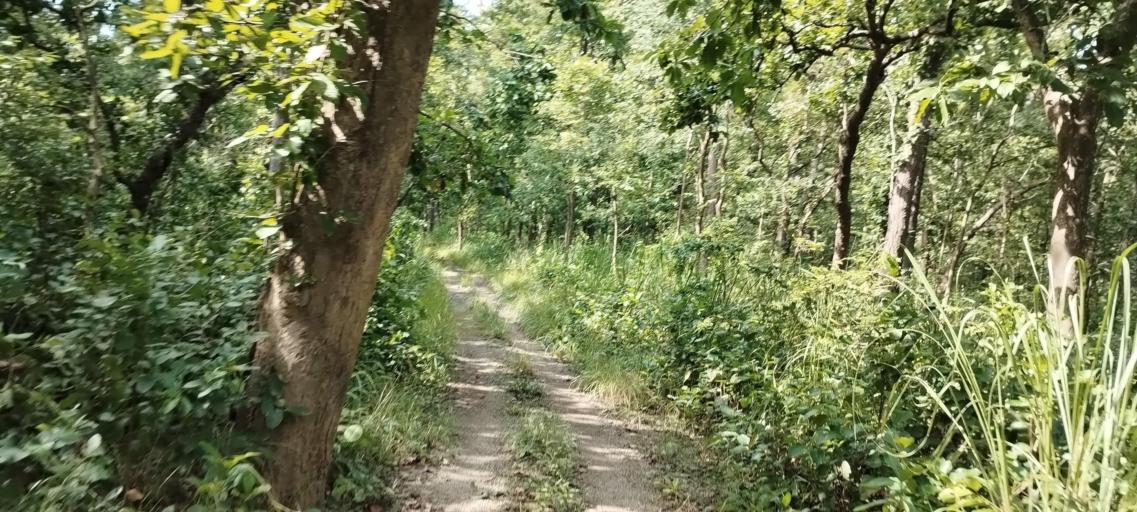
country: NP
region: Far Western
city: Tikapur
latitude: 28.5640
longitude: 81.2938
